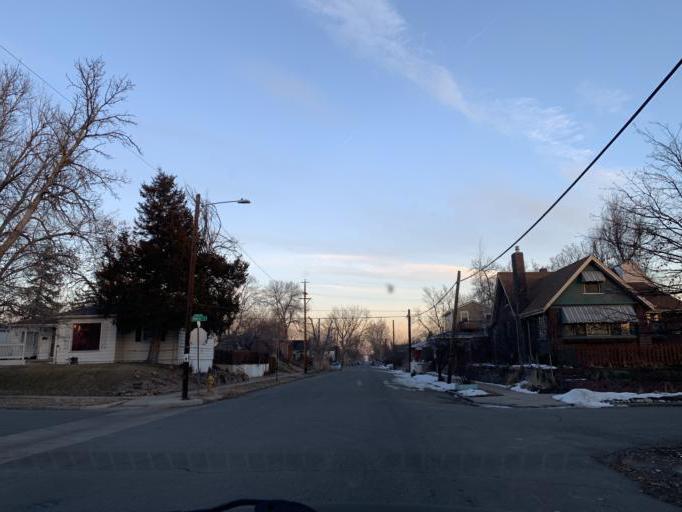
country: US
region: Colorado
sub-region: Adams County
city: Berkley
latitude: 39.7856
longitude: -105.0395
